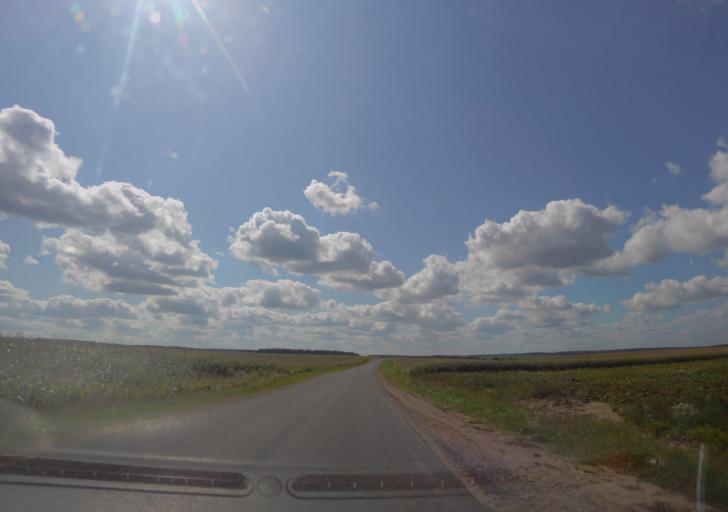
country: BY
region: Minsk
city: Horad Barysaw
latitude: 54.3820
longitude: 28.4801
